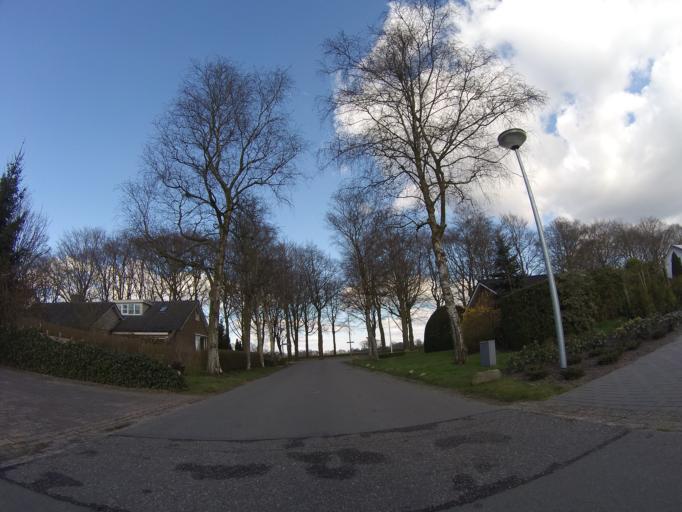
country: NL
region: Drenthe
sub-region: Gemeente Coevorden
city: Sleen
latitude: 52.7703
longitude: 6.8052
